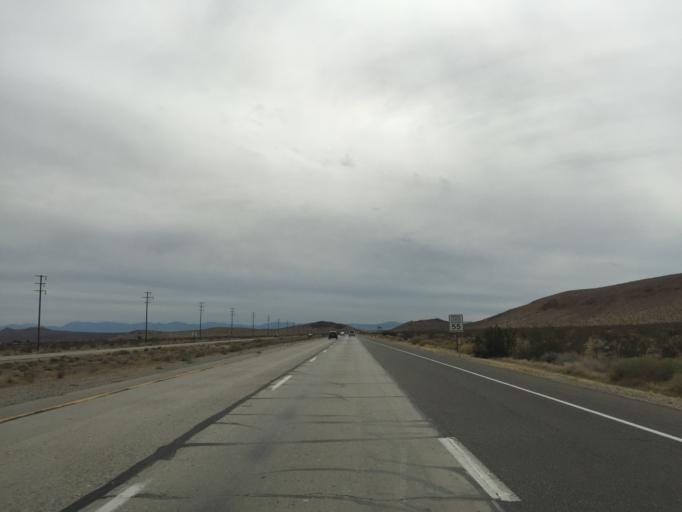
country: US
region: California
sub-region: Kern County
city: Mojave
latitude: 34.9907
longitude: -118.1596
